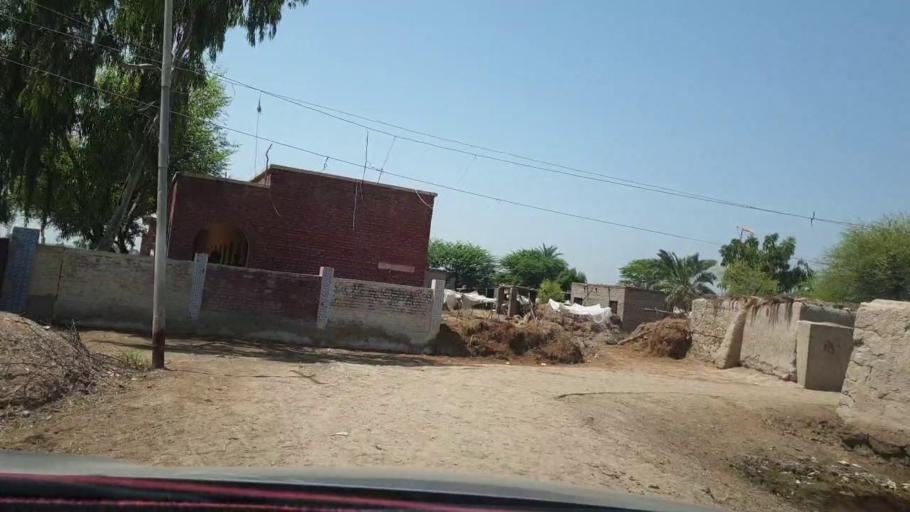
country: PK
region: Sindh
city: Warah
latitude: 27.5016
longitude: 67.7785
